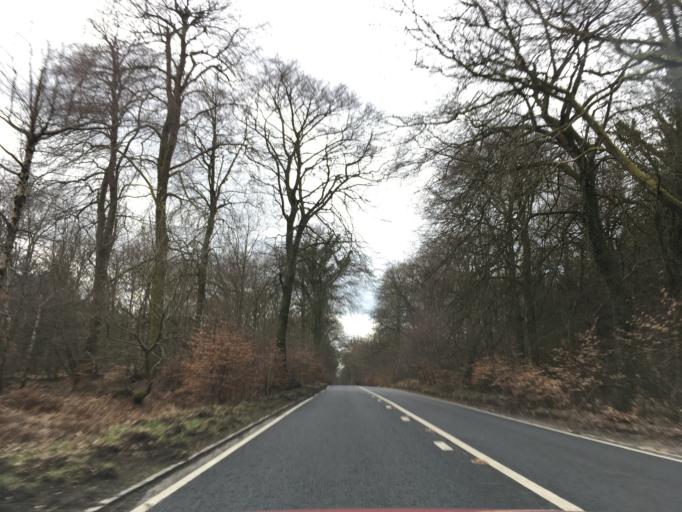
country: GB
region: England
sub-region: Gloucestershire
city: Coleford
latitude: 51.8141
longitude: -2.5955
